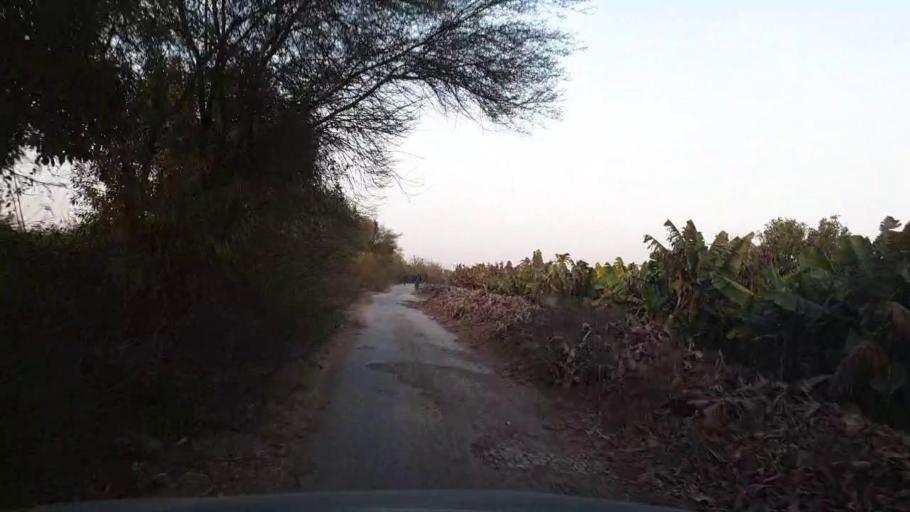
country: PK
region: Sindh
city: Matiari
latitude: 25.5949
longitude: 68.4780
